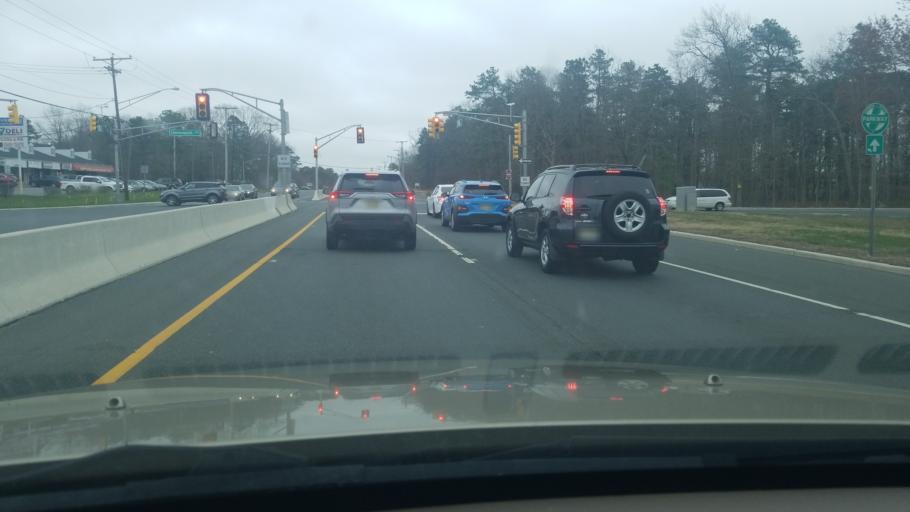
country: US
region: New Jersey
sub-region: Ocean County
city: Leisure Village West-Pine Lake Park
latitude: 39.9966
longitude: -74.2800
